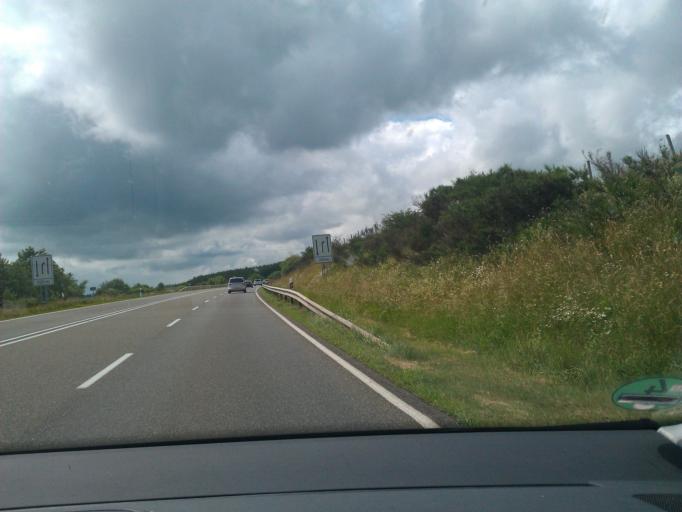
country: DE
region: Rheinland-Pfalz
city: Habscheid
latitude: 50.1986
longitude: 6.2634
